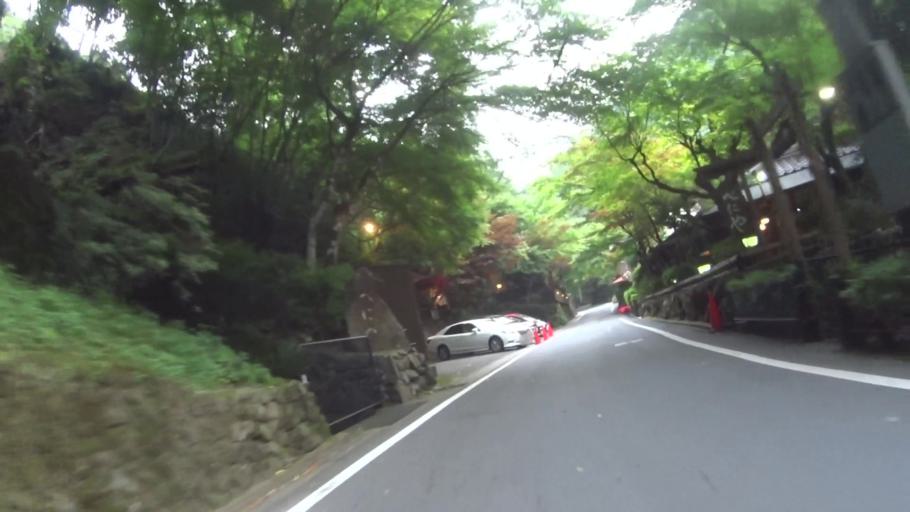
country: JP
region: Kyoto
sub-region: Kyoto-shi
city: Kamigyo-ku
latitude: 35.1168
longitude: 135.7606
